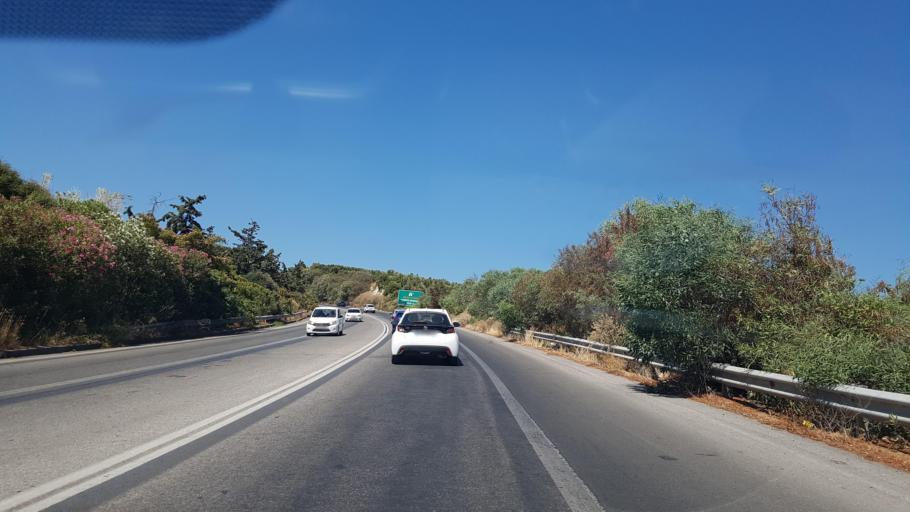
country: GR
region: Crete
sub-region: Nomos Chanias
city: Gerani
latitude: 35.5171
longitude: 23.8416
